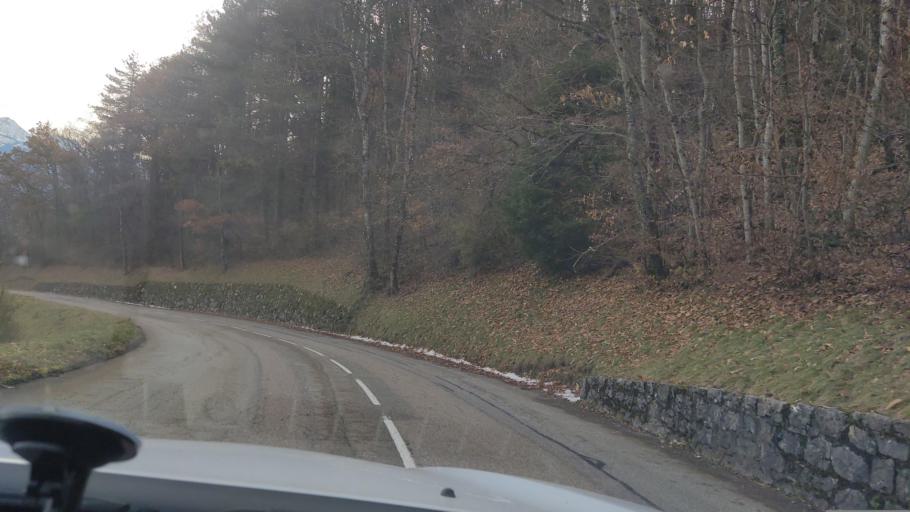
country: FR
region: Rhone-Alpes
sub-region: Departement de la Savoie
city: Coise-Saint-Jean-Pied-Gauthier
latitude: 45.5839
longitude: 6.1519
